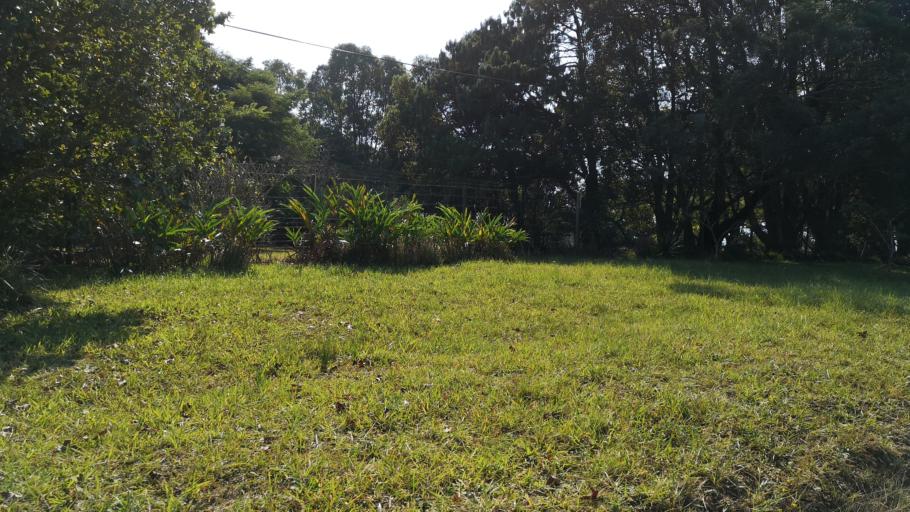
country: ZA
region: KwaZulu-Natal
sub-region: eThekwini Metropolitan Municipality
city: Mpumalanga
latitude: -29.7369
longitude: 30.6823
